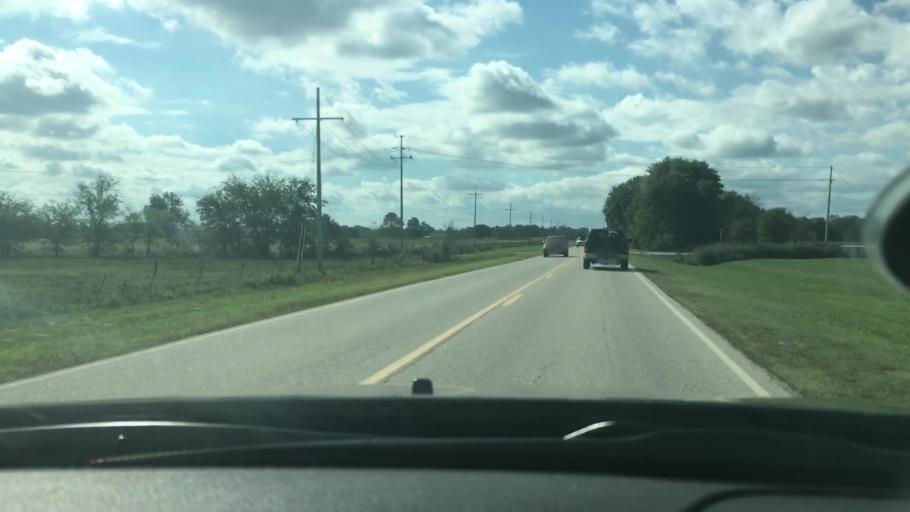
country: US
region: Oklahoma
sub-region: Pontotoc County
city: Ada
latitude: 34.6955
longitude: -96.6349
